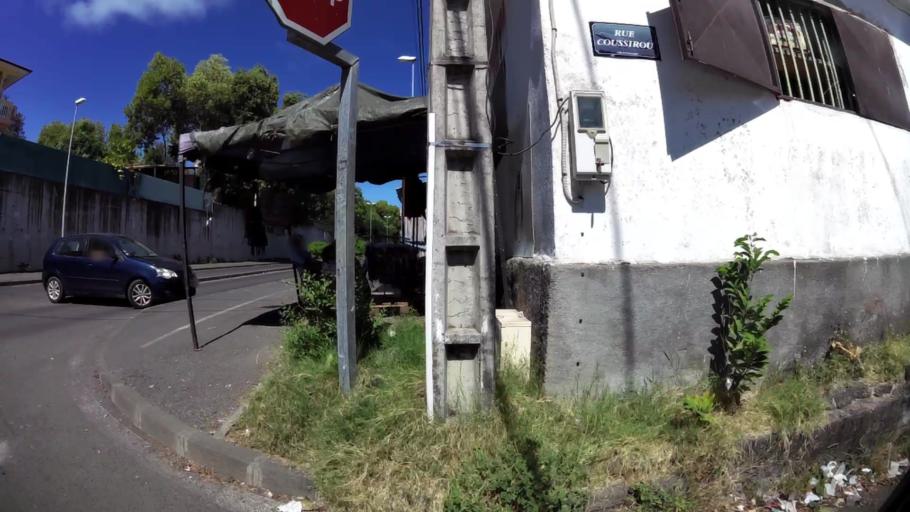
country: YT
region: Pamandzi
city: Pamandzi
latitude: -12.7931
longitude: 45.2824
